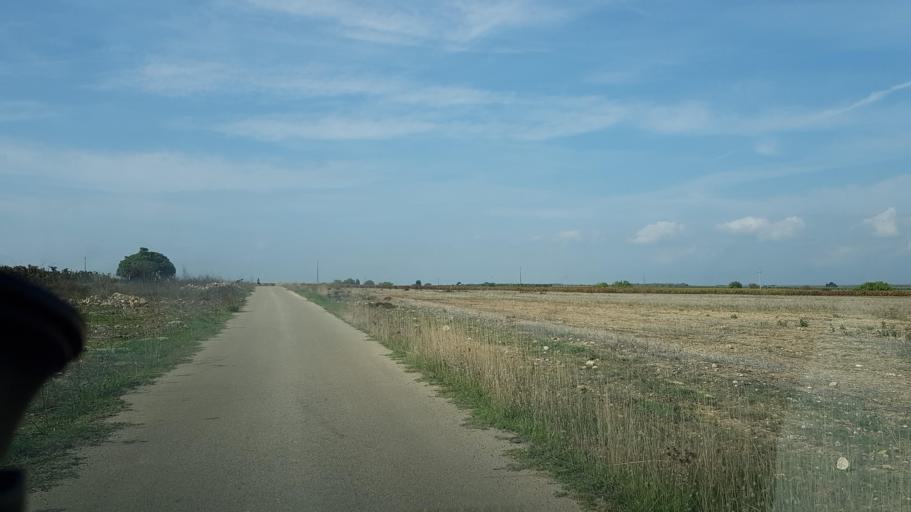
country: IT
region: Apulia
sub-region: Provincia di Brindisi
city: San Pancrazio Salentino
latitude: 40.4304
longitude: 17.8546
